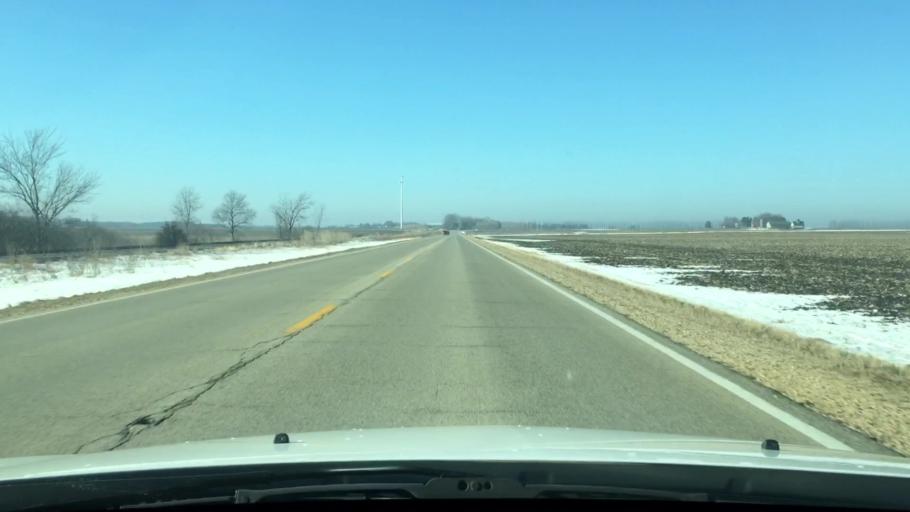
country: US
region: Illinois
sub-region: DeKalb County
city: Waterman
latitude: 41.7688
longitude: -88.8349
